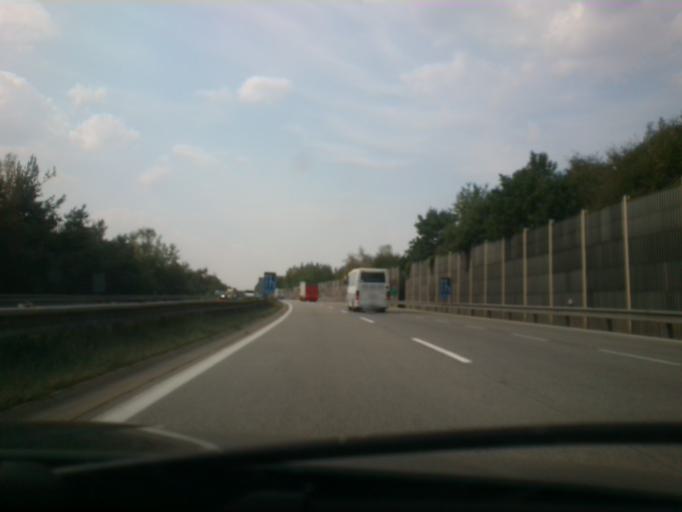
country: CZ
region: Central Bohemia
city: Ondrejov
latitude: 49.8887
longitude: 14.7542
